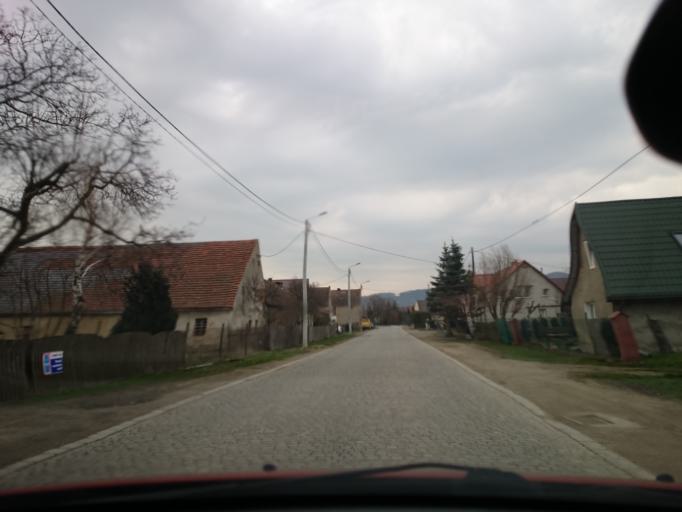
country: PL
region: Lower Silesian Voivodeship
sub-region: Powiat zabkowicki
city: Bardo
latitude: 50.5225
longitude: 16.7767
